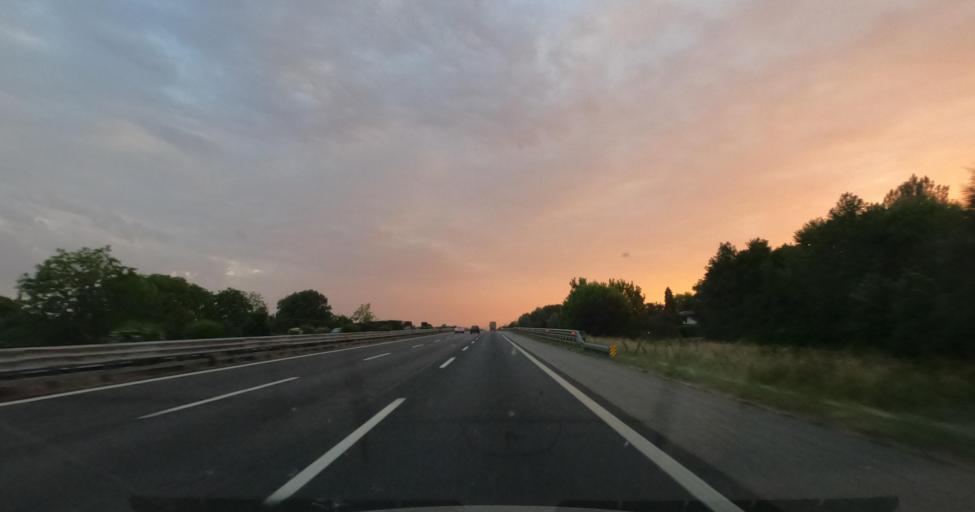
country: IT
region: Veneto
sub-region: Provincia di Padova
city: Vigonza
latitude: 45.4295
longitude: 11.9912
